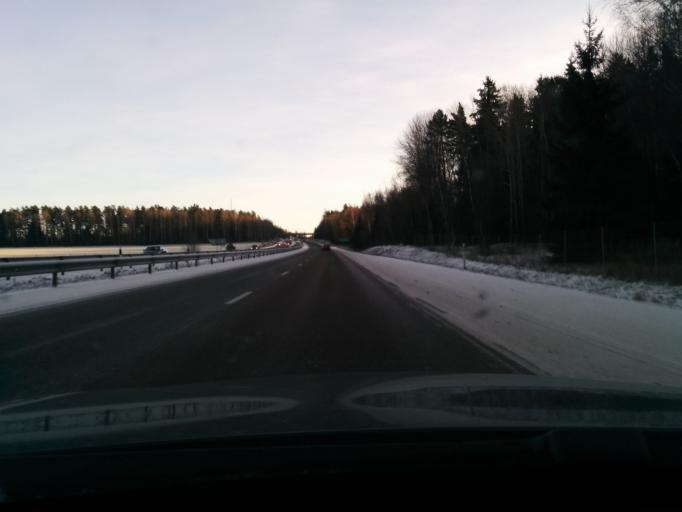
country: SE
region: Uppsala
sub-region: Habo Kommun
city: Balsta
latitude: 59.5850
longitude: 17.5111
